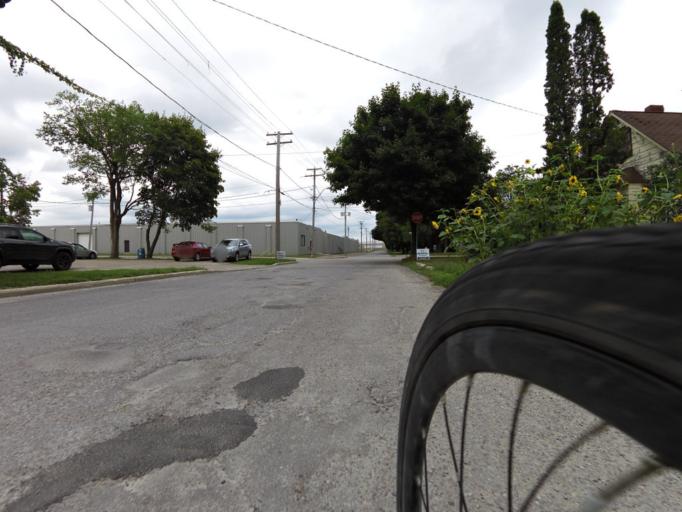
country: CA
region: Ontario
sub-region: Lanark County
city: Smiths Falls
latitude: 44.9015
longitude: -76.0265
